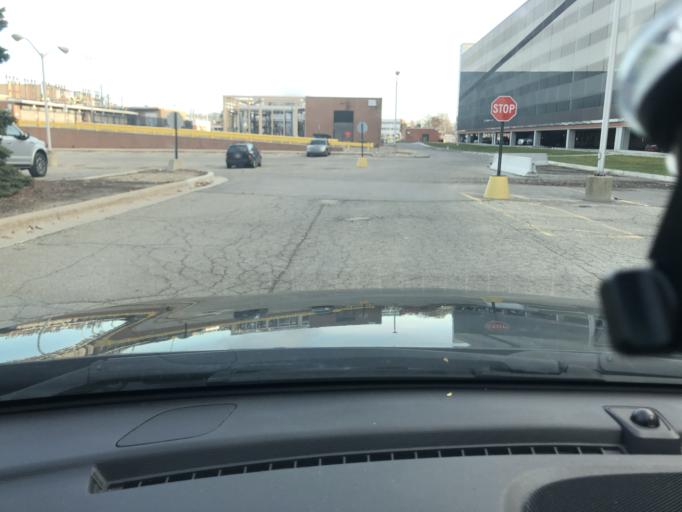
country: US
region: Michigan
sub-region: Wayne County
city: Allen Park
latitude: 42.2955
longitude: -83.2363
